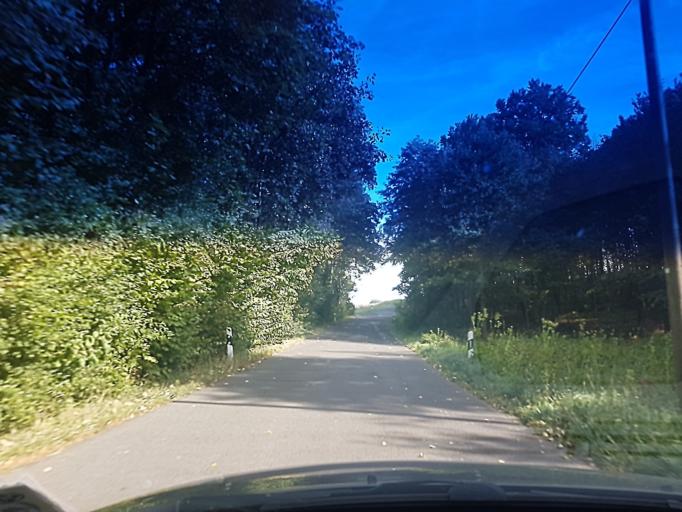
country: DE
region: Bavaria
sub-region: Upper Franconia
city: Schlusselfeld
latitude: 49.7907
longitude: 10.6517
